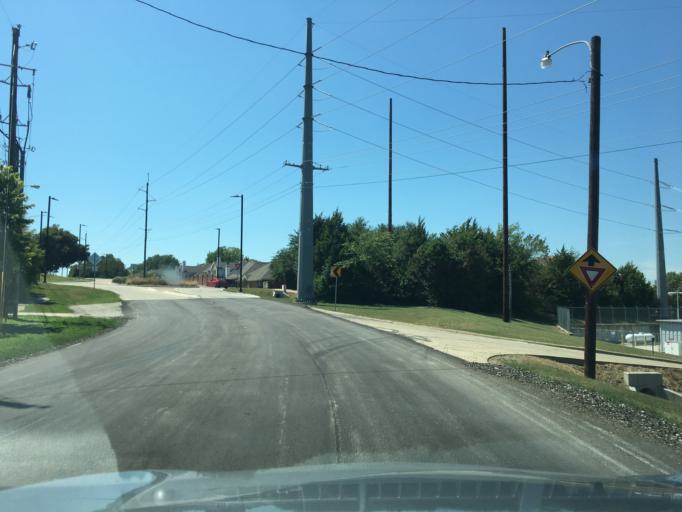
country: US
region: Texas
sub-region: Dallas County
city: Garland
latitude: 32.9518
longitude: -96.6370
